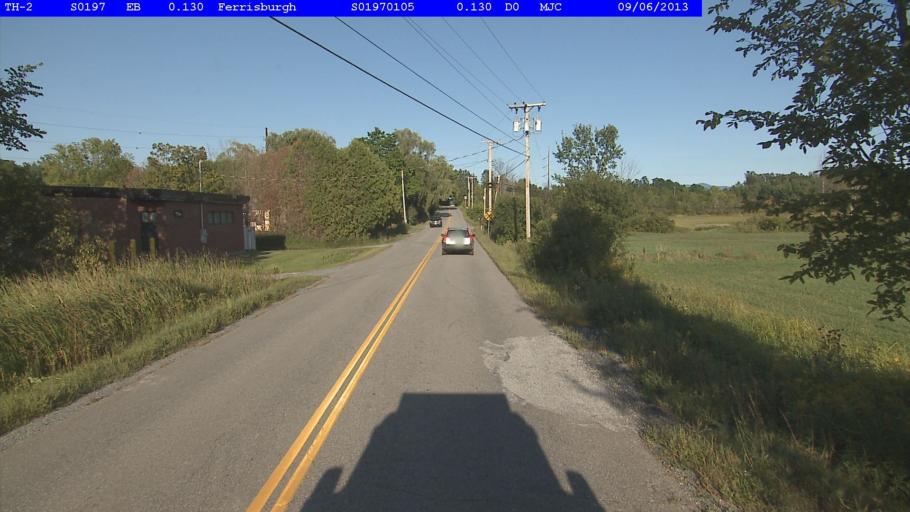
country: US
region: Vermont
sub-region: Addison County
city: Vergennes
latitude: 44.1722
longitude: -73.2364
